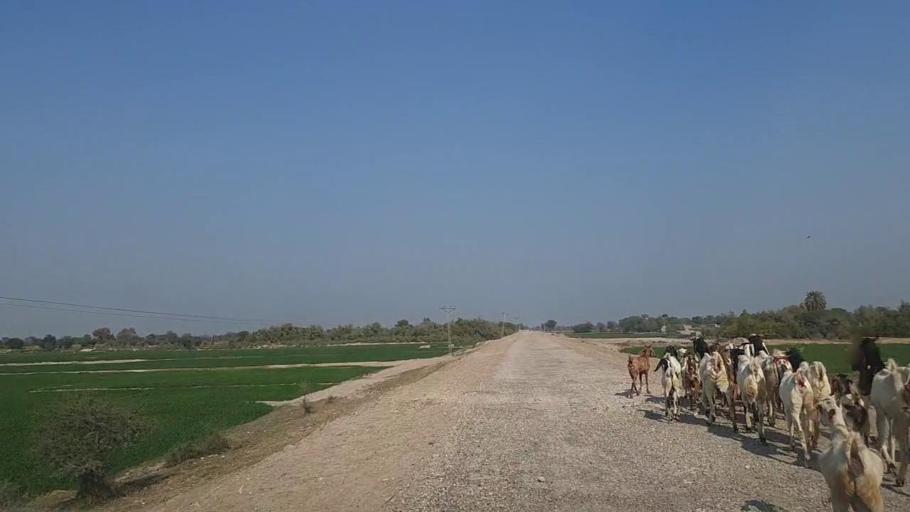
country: PK
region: Sindh
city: Moro
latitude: 26.8001
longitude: 67.9443
